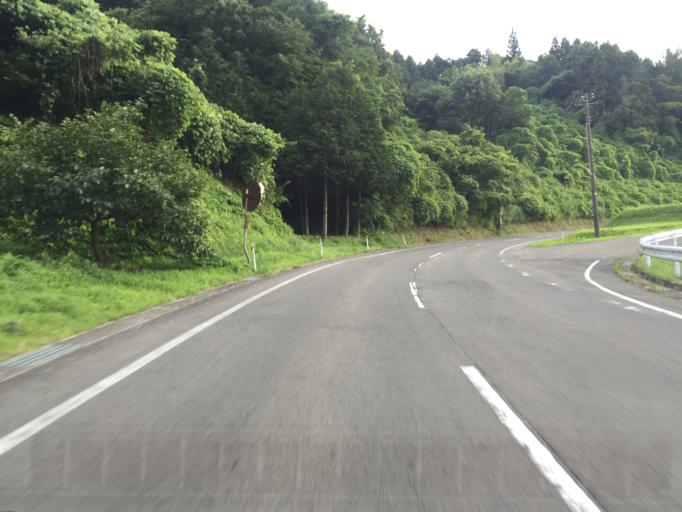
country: JP
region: Fukushima
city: Hobaramachi
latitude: 37.6997
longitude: 140.5783
